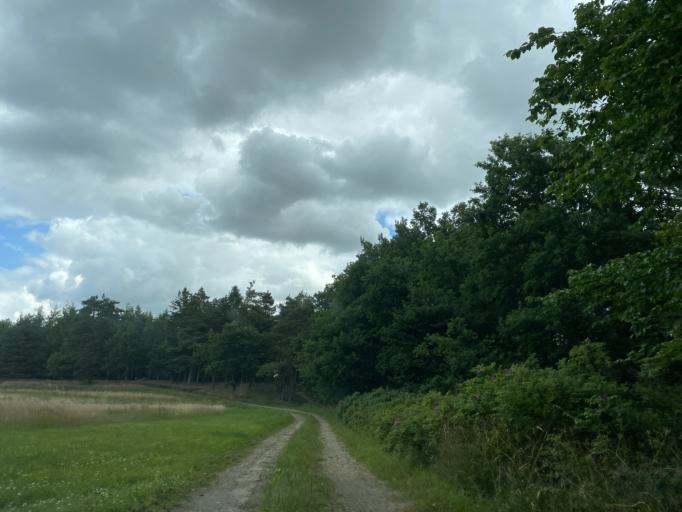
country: DK
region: Central Jutland
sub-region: Viborg Kommune
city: Bjerringbro
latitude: 56.2721
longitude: 9.6544
